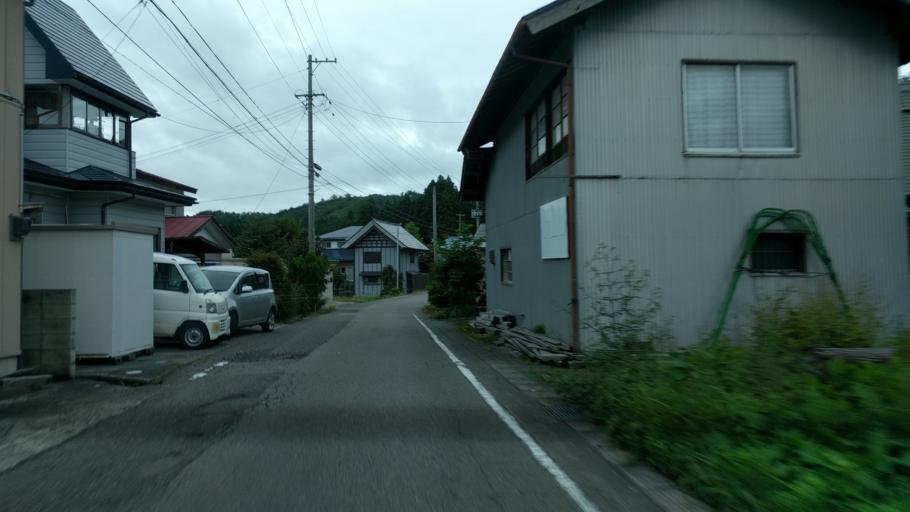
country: JP
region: Fukushima
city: Kitakata
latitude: 37.5436
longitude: 139.7303
